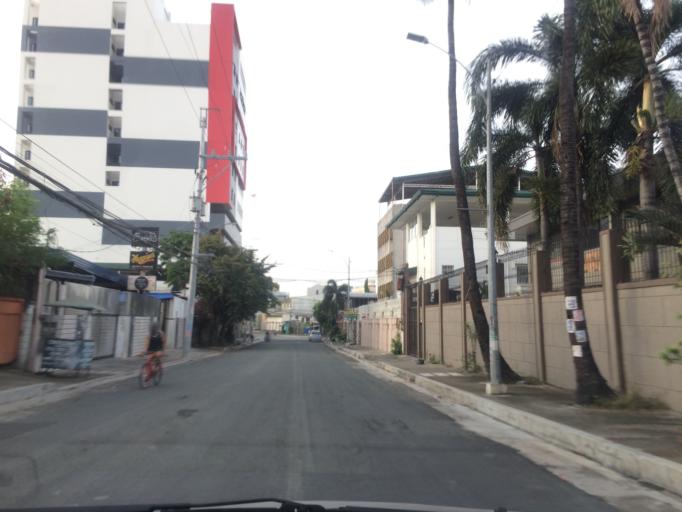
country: PH
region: Calabarzon
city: Del Monte
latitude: 14.6349
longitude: 121.0039
